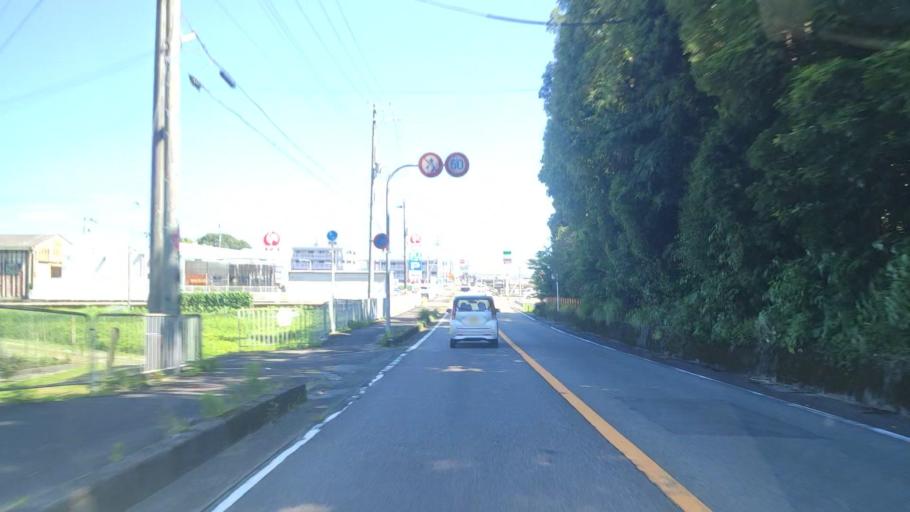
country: JP
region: Wakayama
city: Shingu
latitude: 33.5848
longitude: 135.9189
